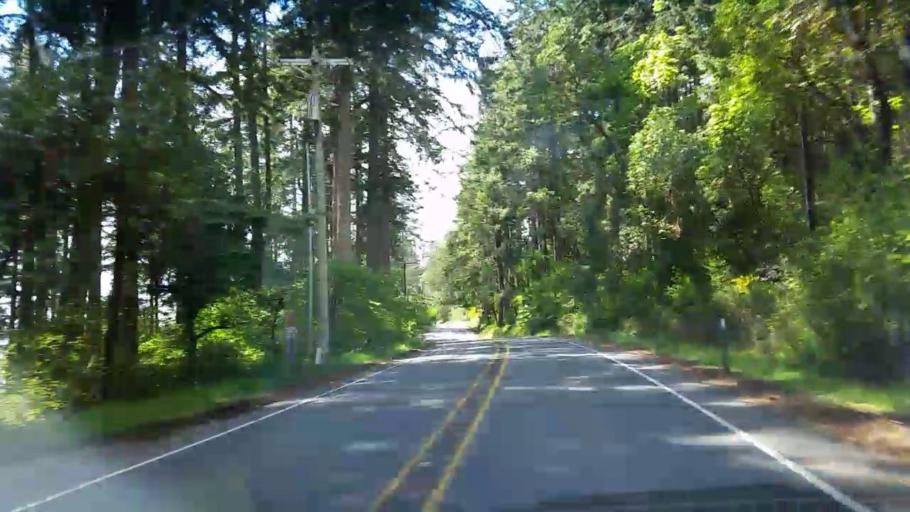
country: US
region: Washington
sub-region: Mason County
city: Allyn
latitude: 47.3617
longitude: -122.7944
